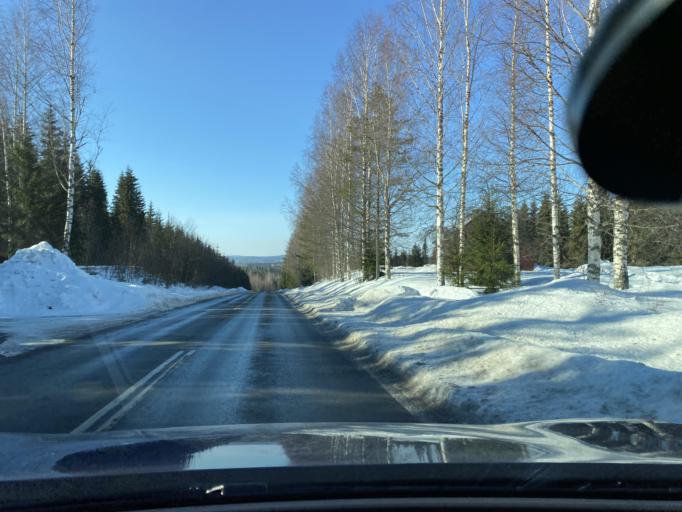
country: FI
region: Central Finland
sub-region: Joutsa
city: Joutsa
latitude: 61.7853
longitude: 26.0684
